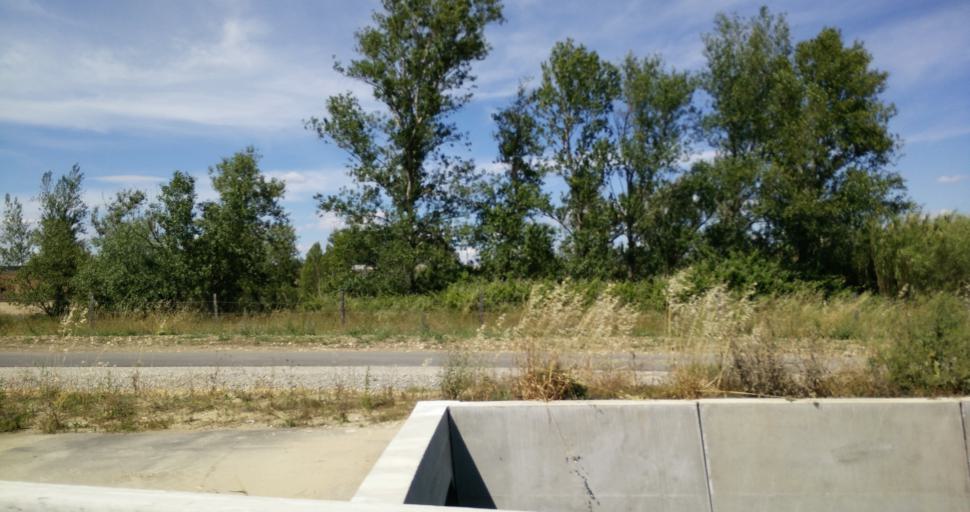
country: FR
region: Languedoc-Roussillon
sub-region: Departement du Gard
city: Vestric-et-Candiac
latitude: 43.7202
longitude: 4.2610
